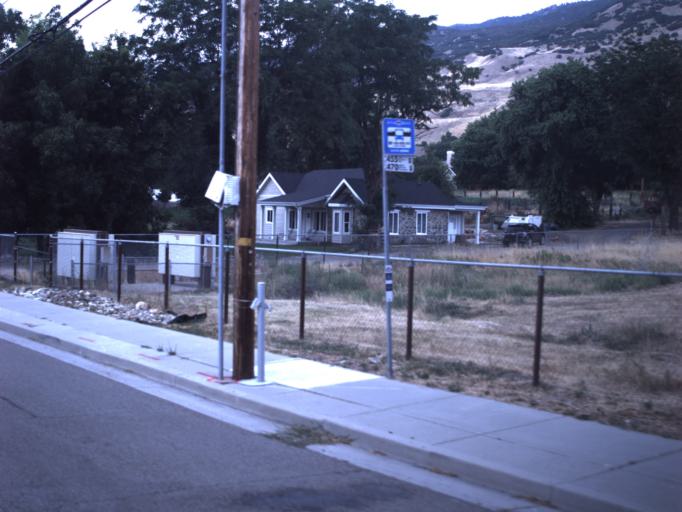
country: US
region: Utah
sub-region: Davis County
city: Centerville
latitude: 40.9402
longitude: -111.8798
